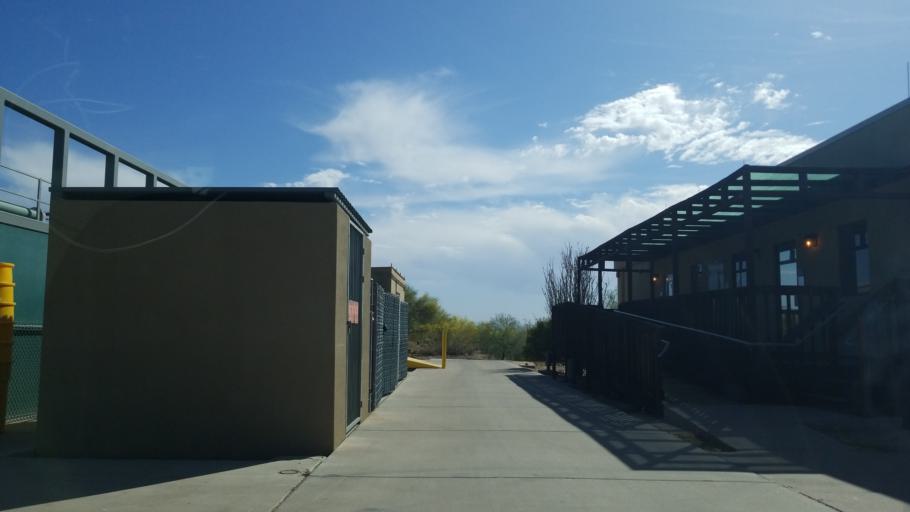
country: US
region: Arizona
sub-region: Maricopa County
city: Fountain Hills
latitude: 33.5871
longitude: -111.7947
